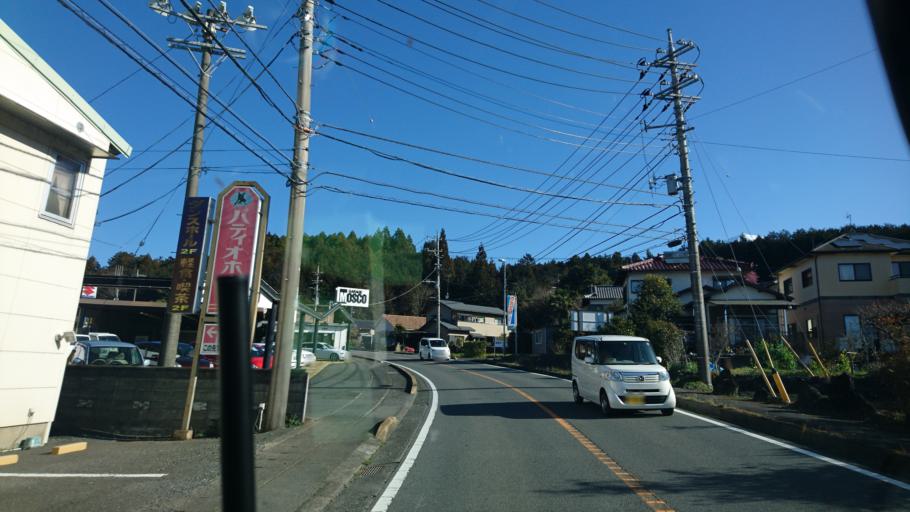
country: JP
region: Shizuoka
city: Fujinomiya
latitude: 35.2687
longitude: 138.6047
